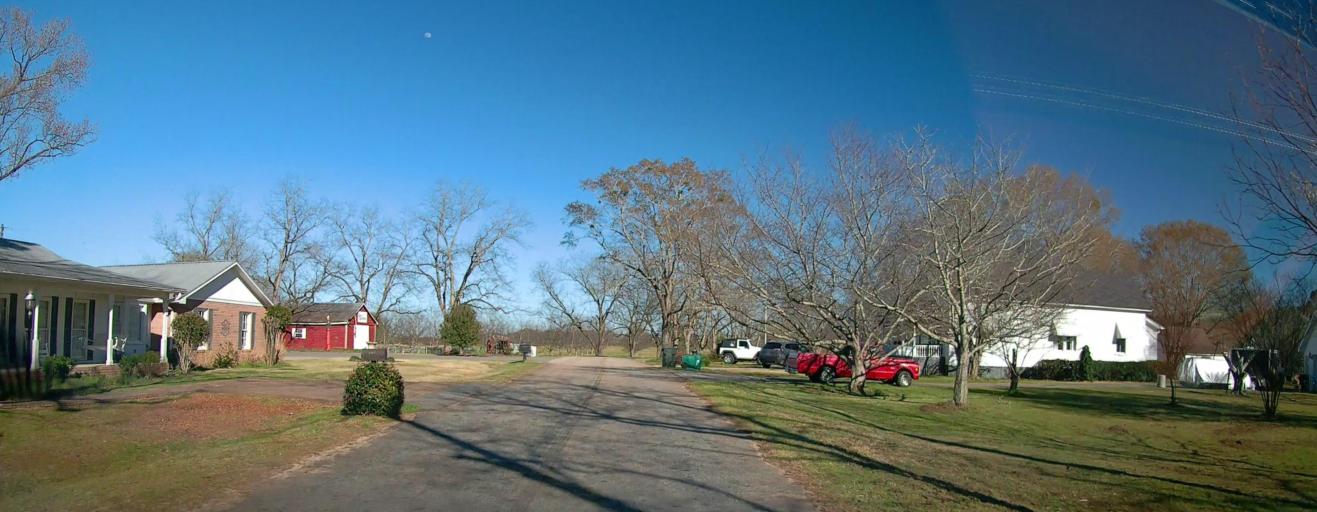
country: US
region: Georgia
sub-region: Peach County
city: Fort Valley
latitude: 32.6377
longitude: -83.8609
